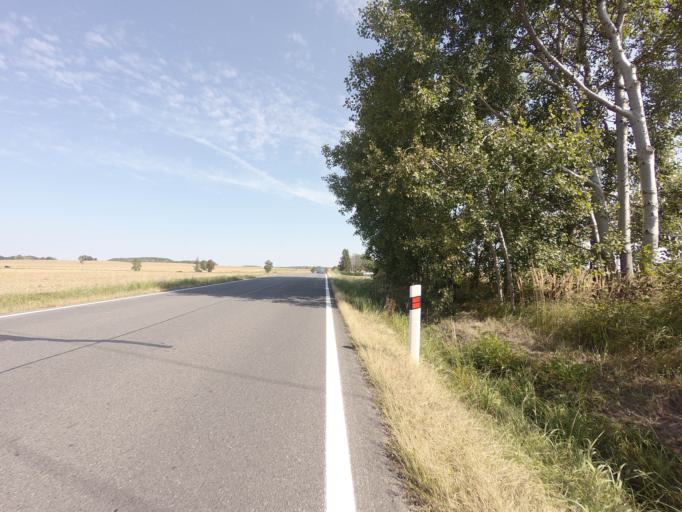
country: CZ
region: Jihocesky
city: Bernartice
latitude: 49.3734
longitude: 14.3794
